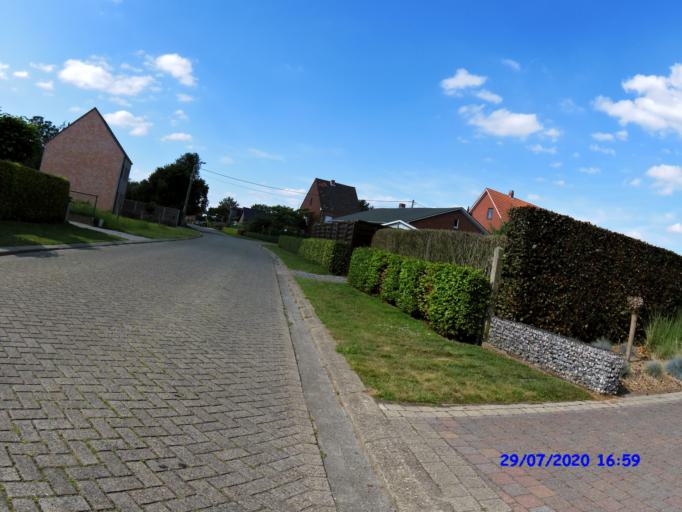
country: BE
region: Flanders
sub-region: Provincie Antwerpen
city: Beerse
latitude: 51.3200
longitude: 4.8420
